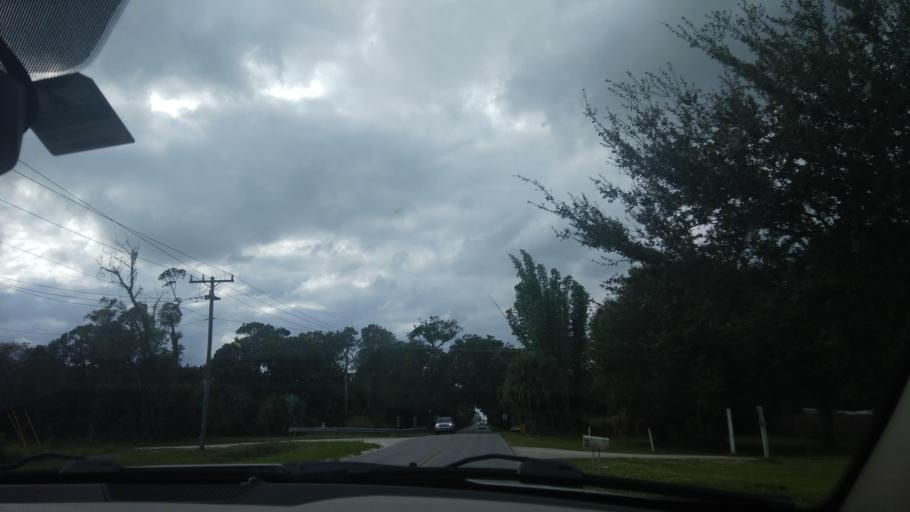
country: US
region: Florida
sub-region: Saint Lucie County
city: Lakewood Park
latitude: 27.5209
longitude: -80.3896
